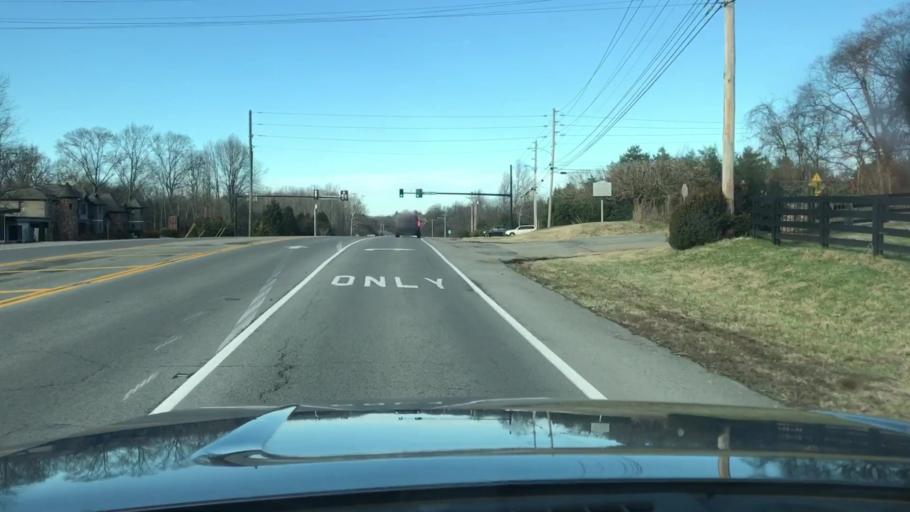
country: US
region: Tennessee
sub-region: Williamson County
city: Brentwood Estates
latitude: 35.9767
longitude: -86.7767
